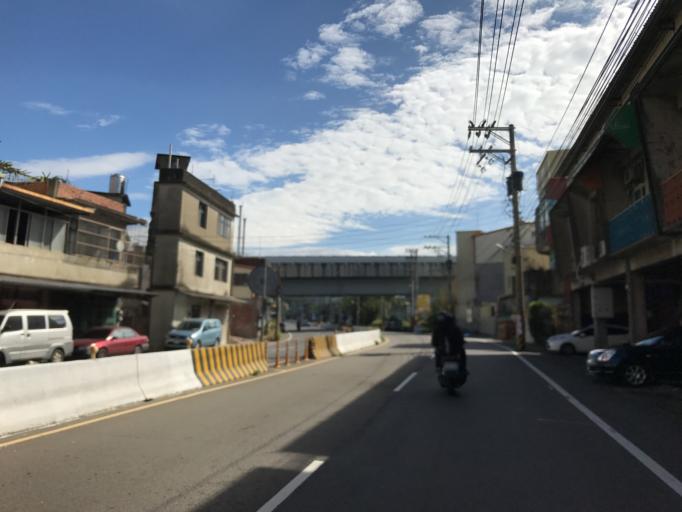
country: TW
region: Taiwan
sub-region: Hsinchu
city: Zhubei
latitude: 24.7777
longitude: 121.0325
